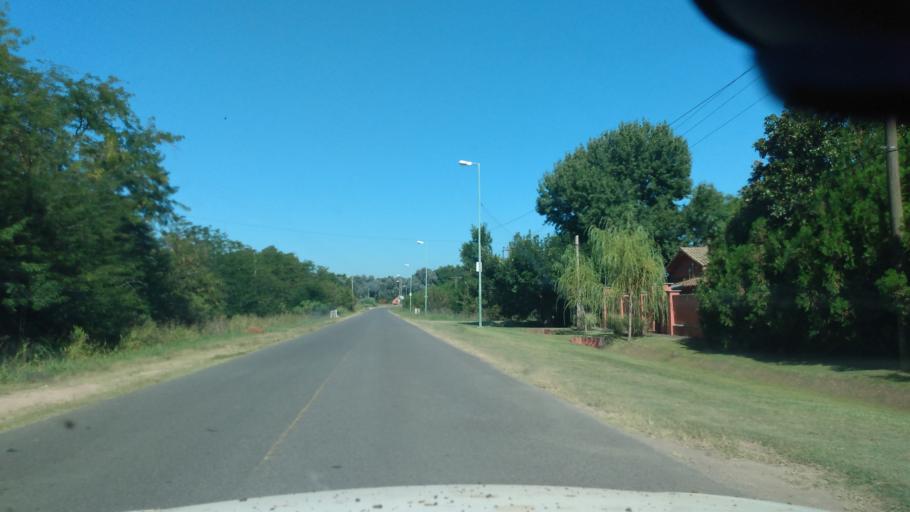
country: AR
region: Buenos Aires
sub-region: Partido de Lujan
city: Lujan
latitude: -34.5083
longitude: -59.0836
